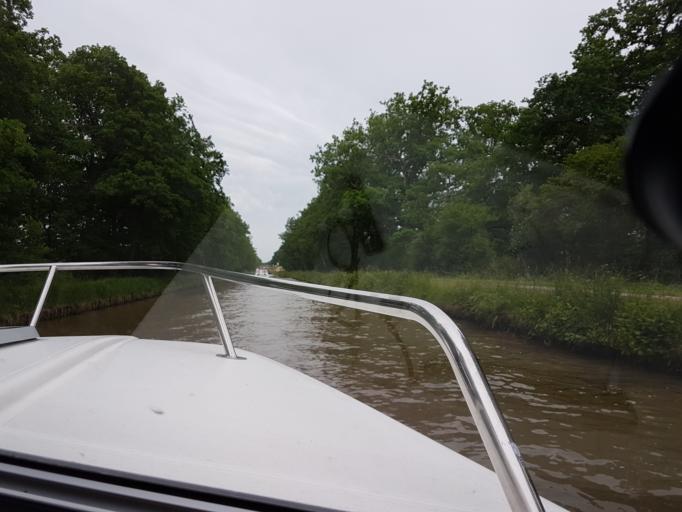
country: FR
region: Bourgogne
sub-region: Departement de la Nievre
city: Clamecy
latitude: 47.3828
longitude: 3.6019
